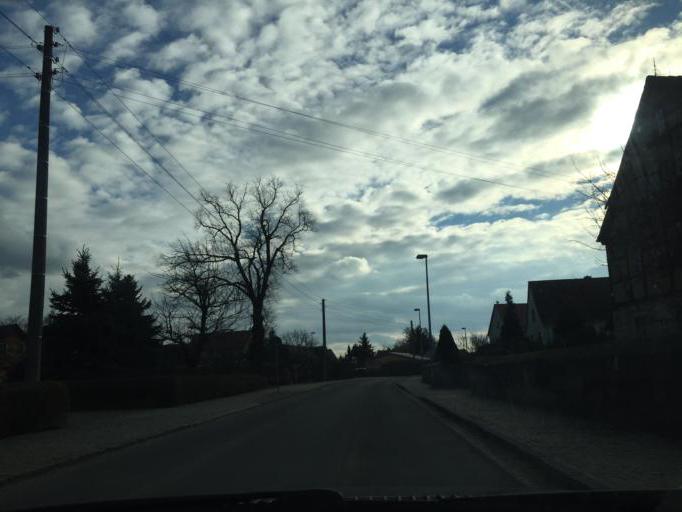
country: DE
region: Saxony
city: Ebersbach
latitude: 51.2492
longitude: 13.6608
